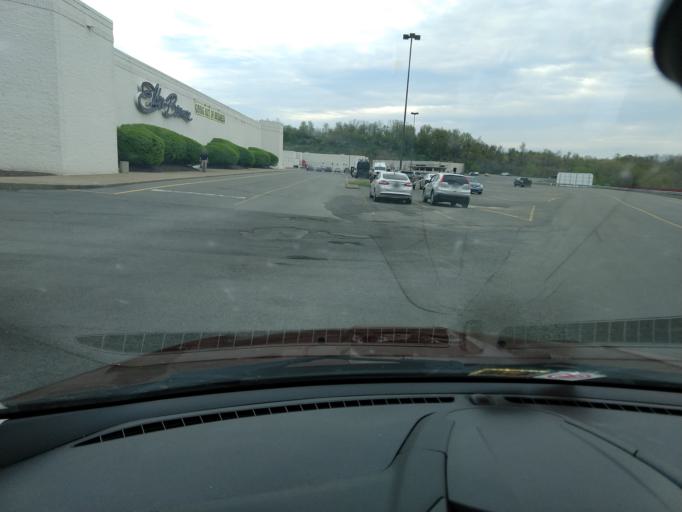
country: US
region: West Virginia
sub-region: Harrison County
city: Bridgeport
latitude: 39.3112
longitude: -80.2728
